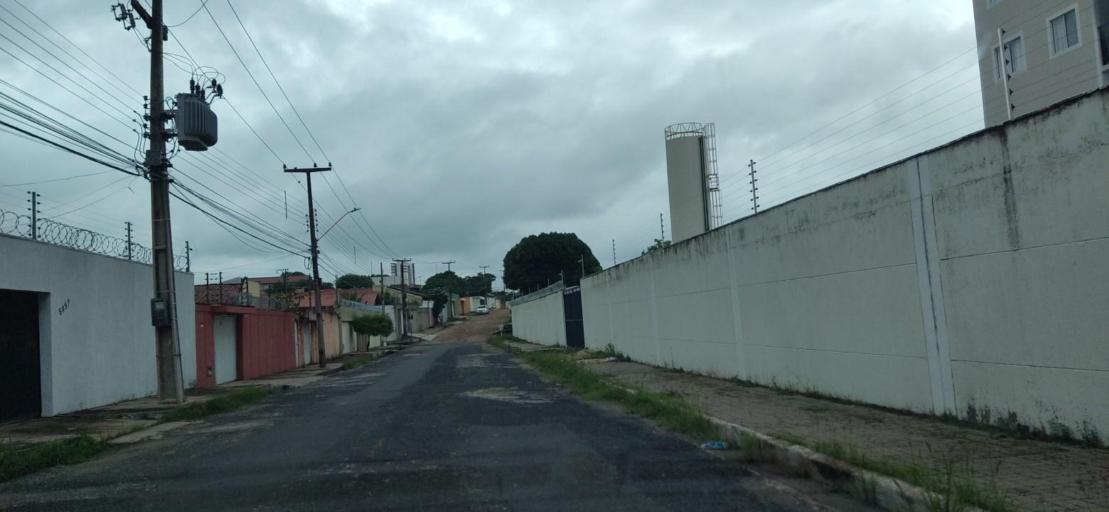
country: BR
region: Piaui
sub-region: Teresina
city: Teresina
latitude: -5.0718
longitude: -42.7568
